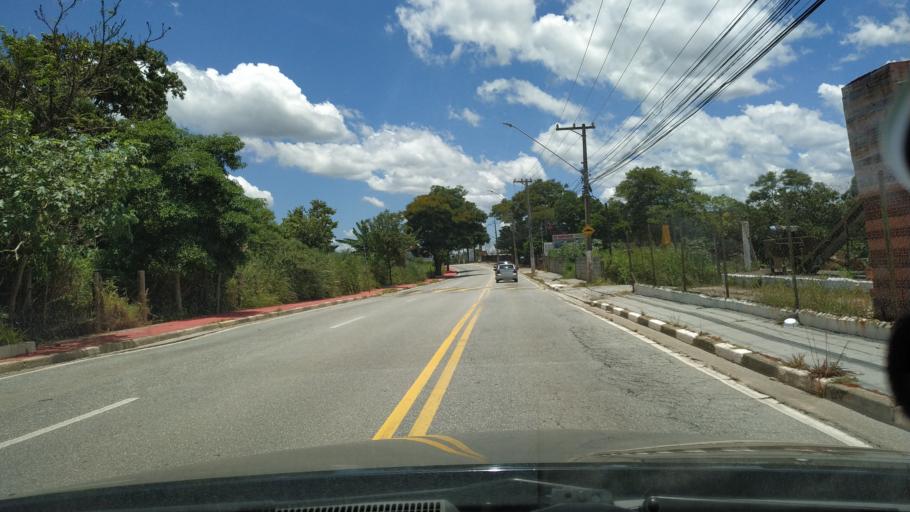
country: BR
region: Sao Paulo
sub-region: Santana De Parnaiba
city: Santana de Parnaiba
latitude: -23.4525
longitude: -46.8994
